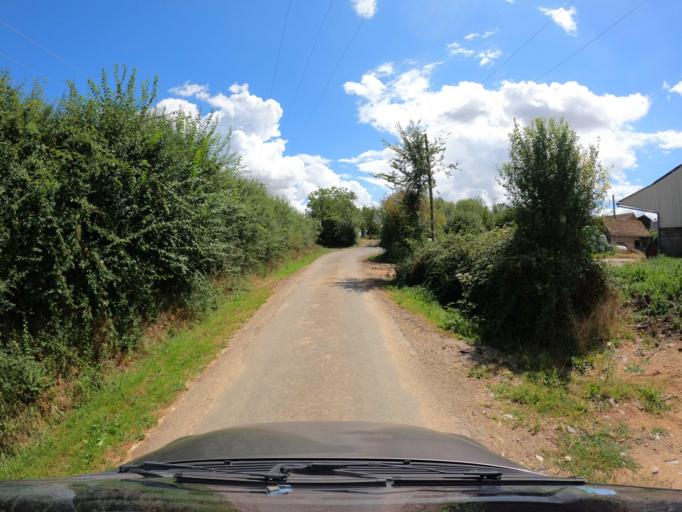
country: FR
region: Pays de la Loire
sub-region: Departement de la Sarthe
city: Brulon
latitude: 47.9420
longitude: -0.2346
